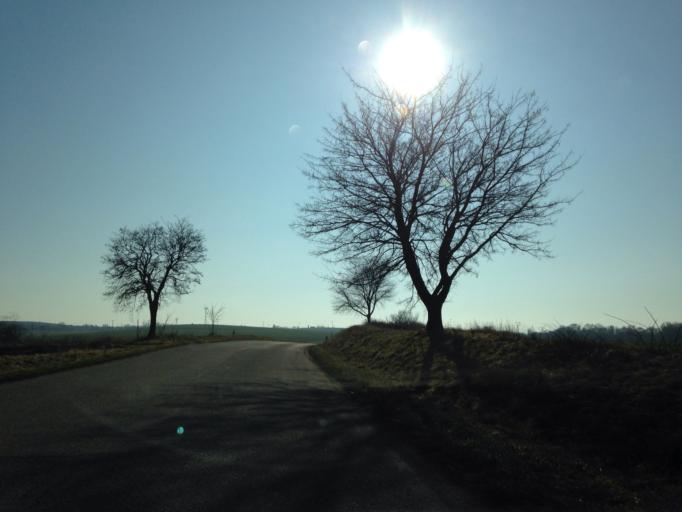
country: SK
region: Nitriansky
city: Svodin
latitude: 47.9168
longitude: 18.4065
